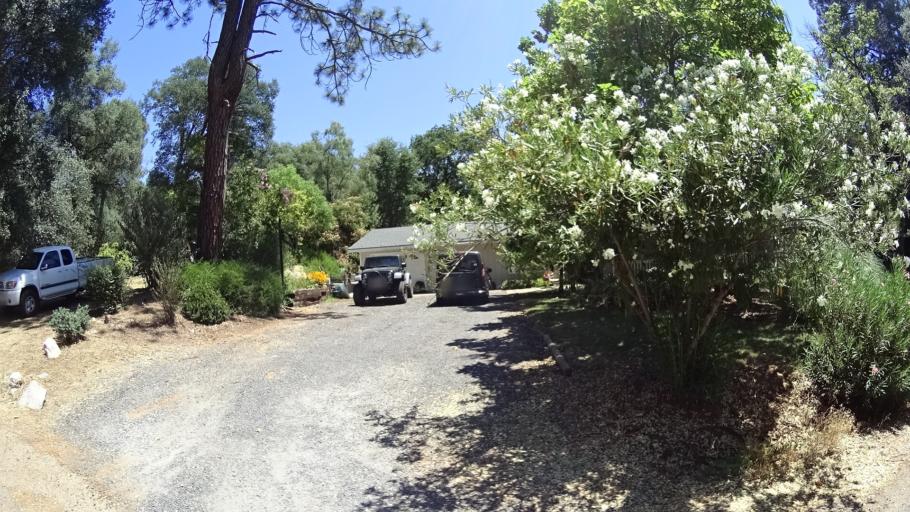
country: US
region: California
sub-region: Calaveras County
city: Murphys
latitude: 38.1346
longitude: -120.4511
